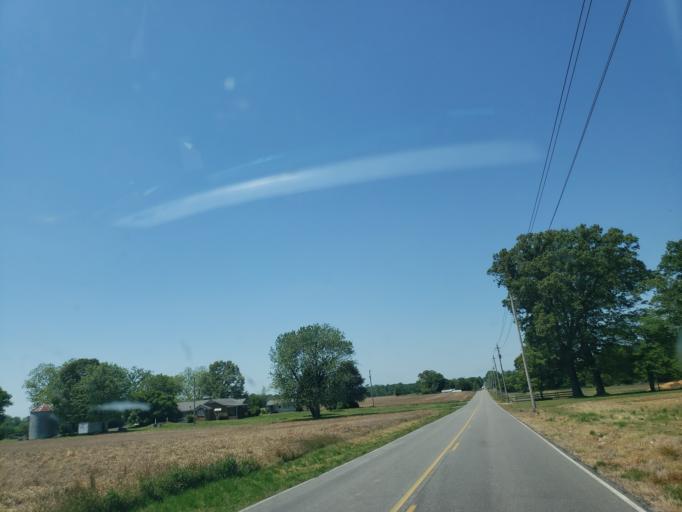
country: US
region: Alabama
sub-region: Madison County
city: Hazel Green
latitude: 34.9621
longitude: -86.6442
